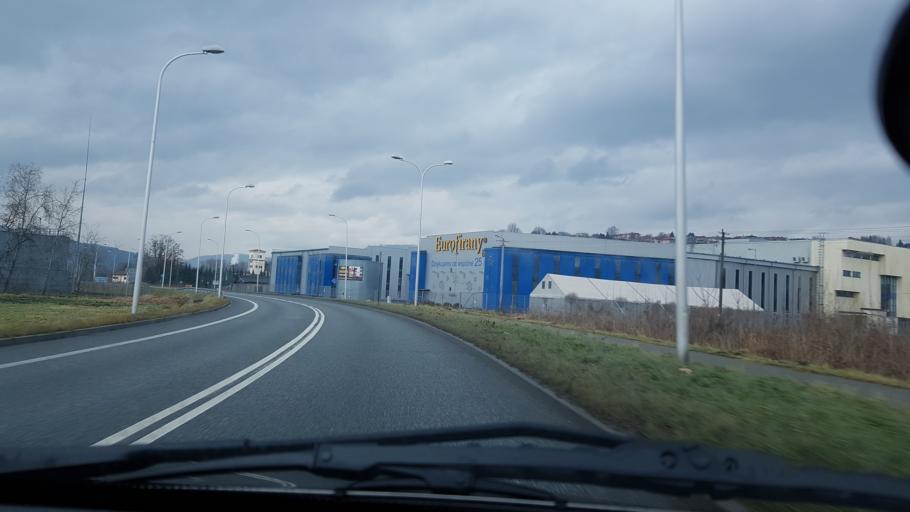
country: PL
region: Silesian Voivodeship
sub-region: Powiat zywiecki
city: Zywiec
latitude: 49.6949
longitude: 19.1990
